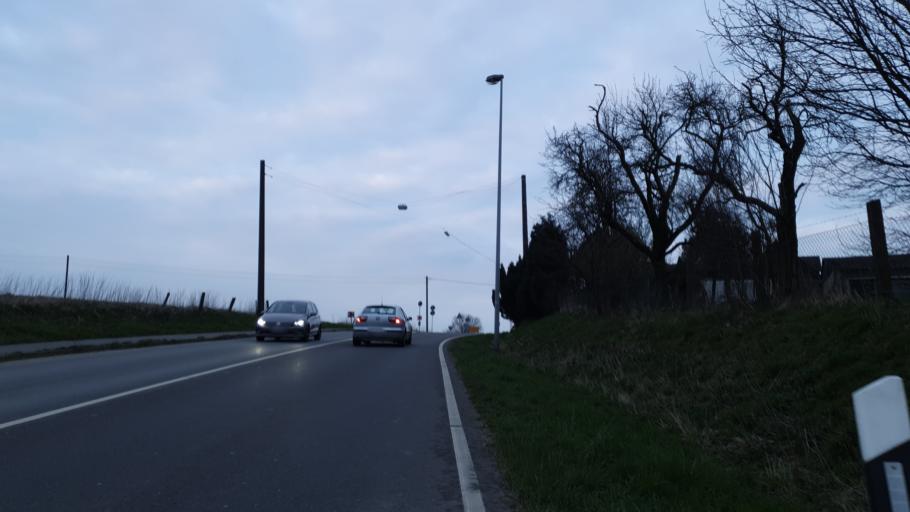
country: DE
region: North Rhine-Westphalia
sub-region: Regierungsbezirk Koln
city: Odenthal
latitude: 51.0627
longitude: 7.1133
